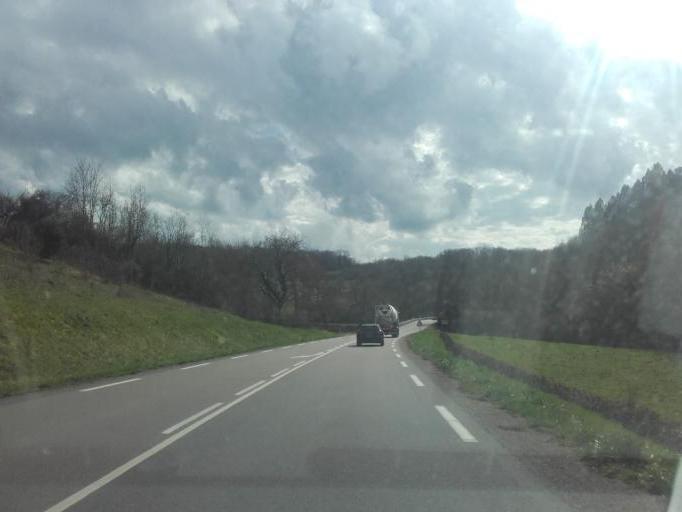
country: FR
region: Bourgogne
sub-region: Departement de la Cote-d'Or
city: Nolay
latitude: 46.9625
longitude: 4.6910
